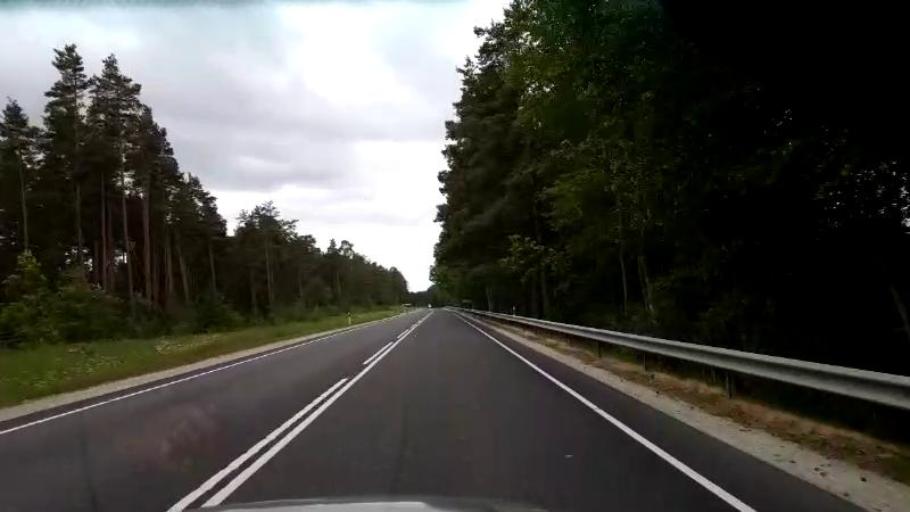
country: EE
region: Paernumaa
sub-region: Paernu linn
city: Parnu
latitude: 58.2682
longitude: 24.5534
